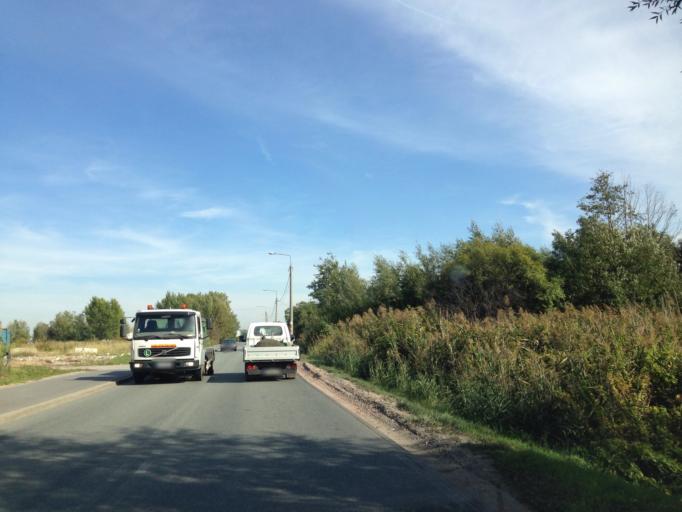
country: PL
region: Masovian Voivodeship
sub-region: Powiat warszawski zachodni
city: Ozarow Mazowiecki
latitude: 52.1803
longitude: 20.7750
